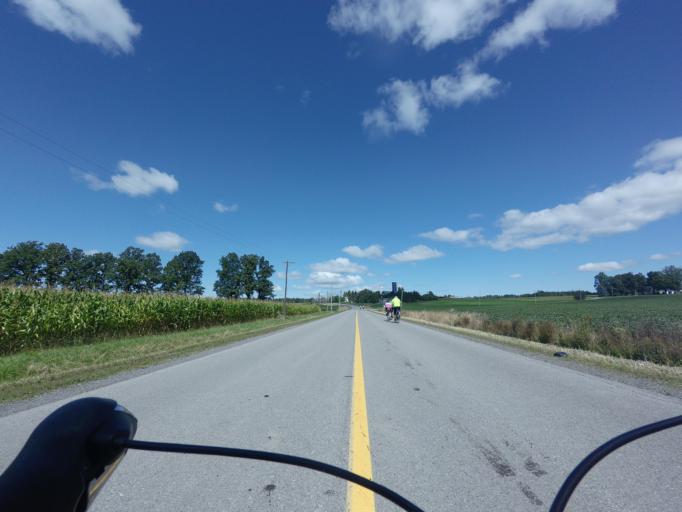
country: CA
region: Ontario
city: Bells Corners
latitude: 45.2574
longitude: -75.8094
